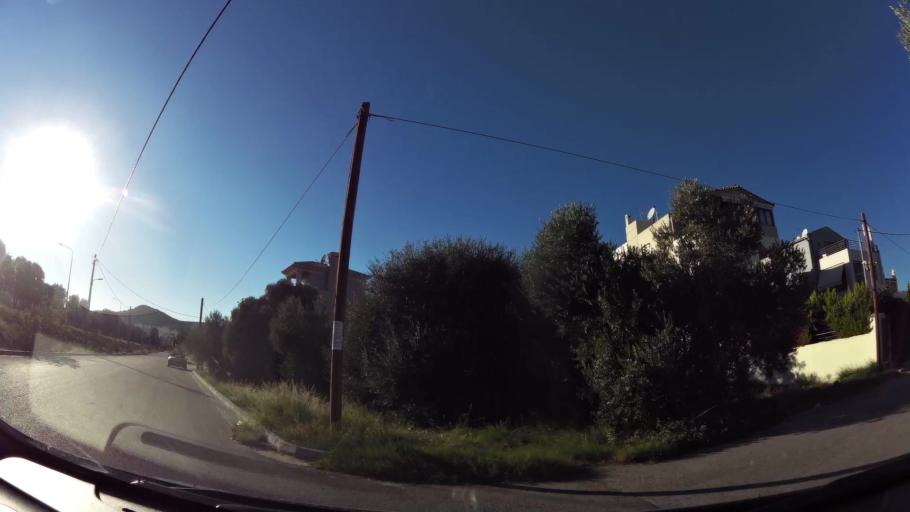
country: GR
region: Attica
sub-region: Nomarchia Anatolikis Attikis
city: Vari
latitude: 37.8225
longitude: 23.8111
